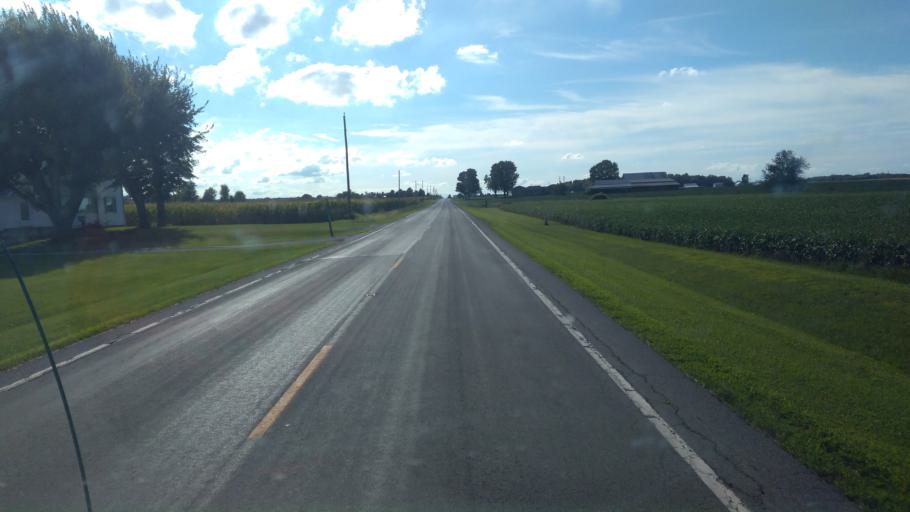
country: US
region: Ohio
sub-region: Hardin County
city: Kenton
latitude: 40.7324
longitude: -83.6846
